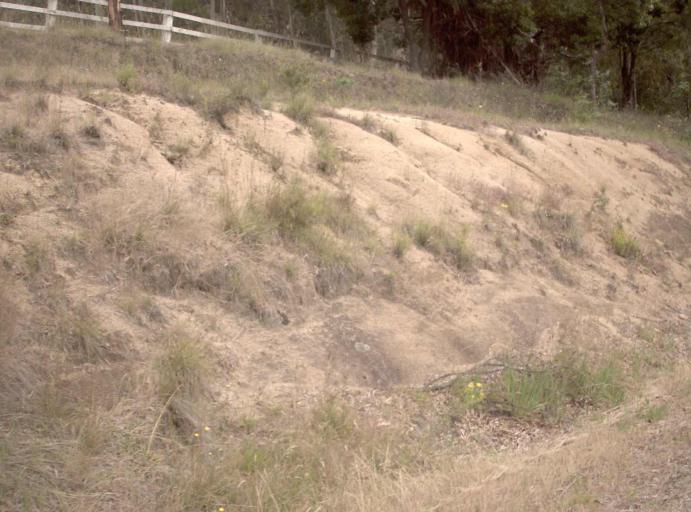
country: AU
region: Victoria
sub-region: East Gippsland
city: Bairnsdale
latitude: -37.5814
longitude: 147.1816
